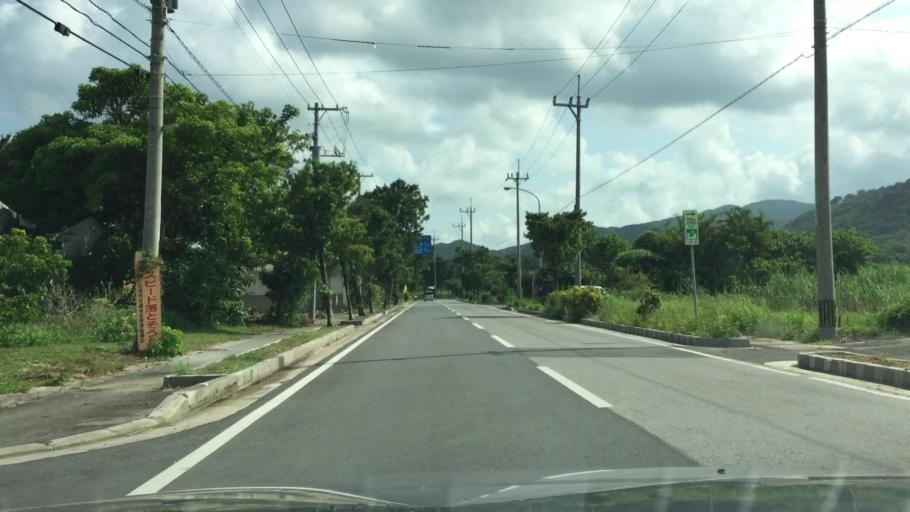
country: JP
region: Okinawa
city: Ishigaki
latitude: 24.4675
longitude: 124.2506
